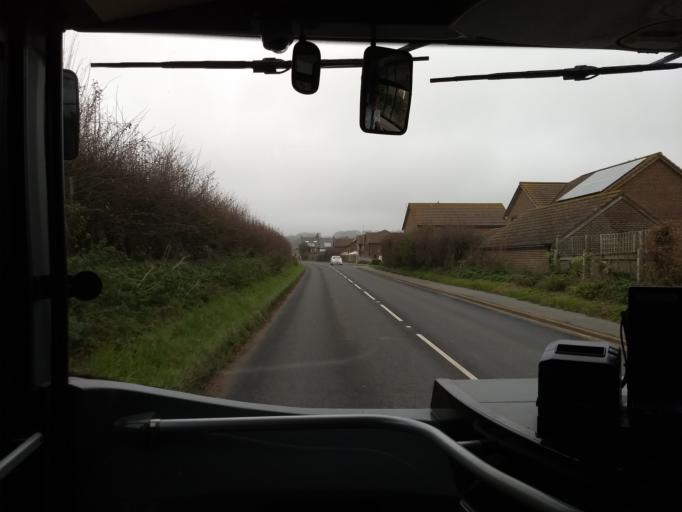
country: GB
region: England
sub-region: Isle of Wight
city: Newchurch
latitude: 50.6723
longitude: -1.2362
